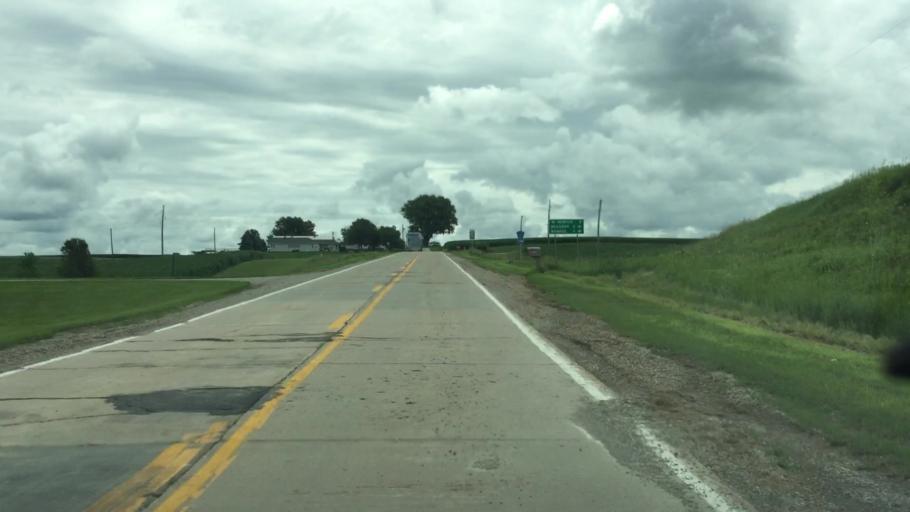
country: US
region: Iowa
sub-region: Jasper County
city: Monroe
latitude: 41.5807
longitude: -93.1004
